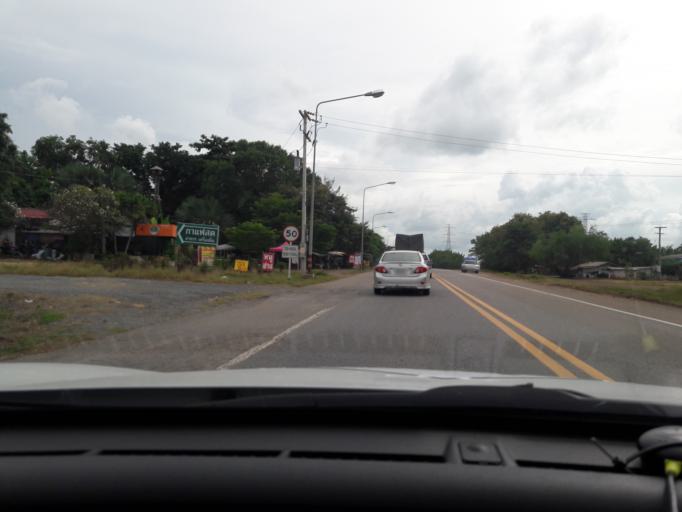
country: TH
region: Nakhon Sawan
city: Tak Fa
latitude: 15.4187
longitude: 100.5161
